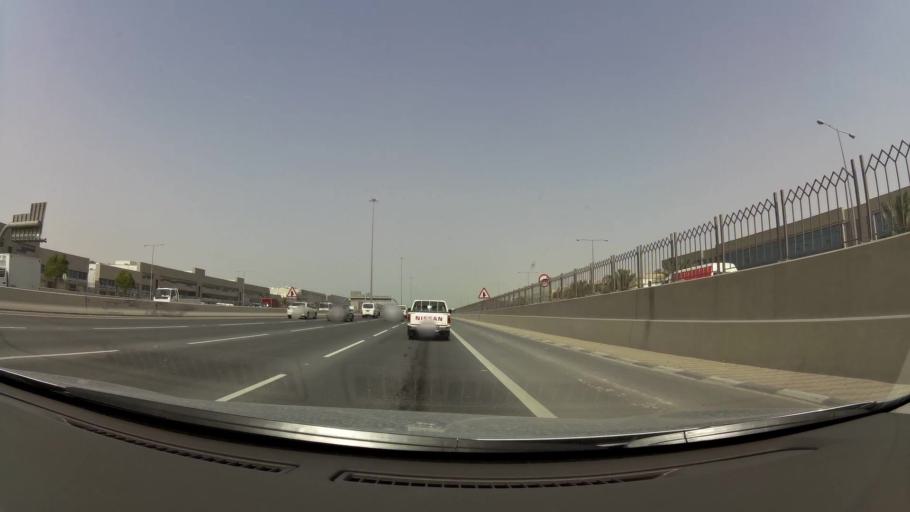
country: QA
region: Baladiyat ad Dawhah
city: Doha
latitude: 25.2507
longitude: 51.4749
